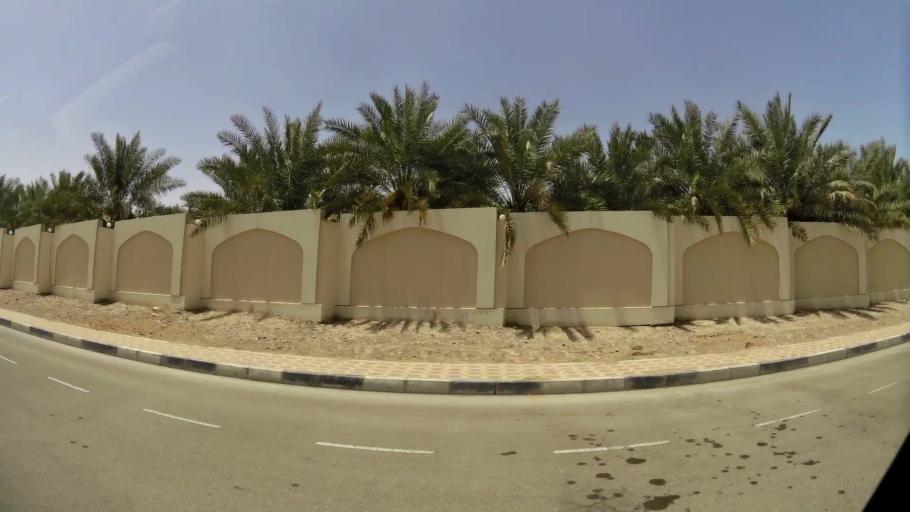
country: OM
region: Al Buraimi
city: Al Buraymi
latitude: 24.2548
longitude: 55.7160
